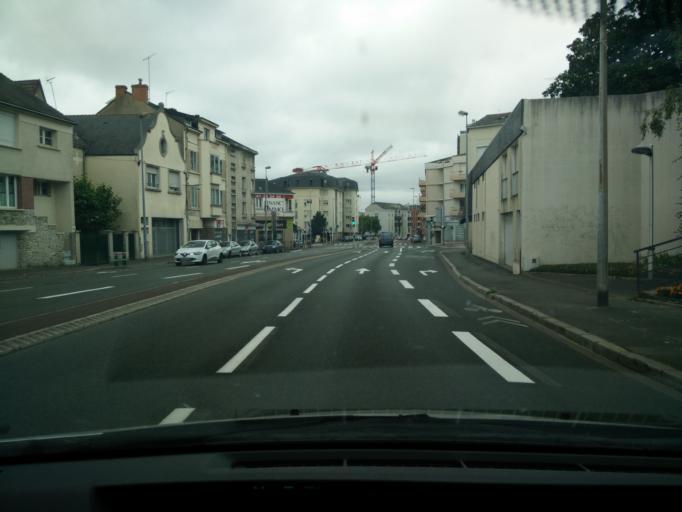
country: FR
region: Pays de la Loire
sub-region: Departement de Maine-et-Loire
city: Angers
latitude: 47.4720
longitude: -0.5399
